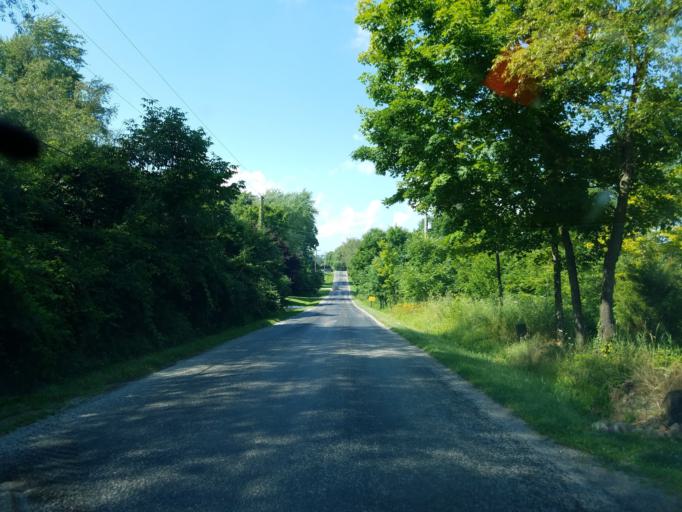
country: US
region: Ohio
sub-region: Ashland County
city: Ashland
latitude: 40.8894
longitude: -82.3490
